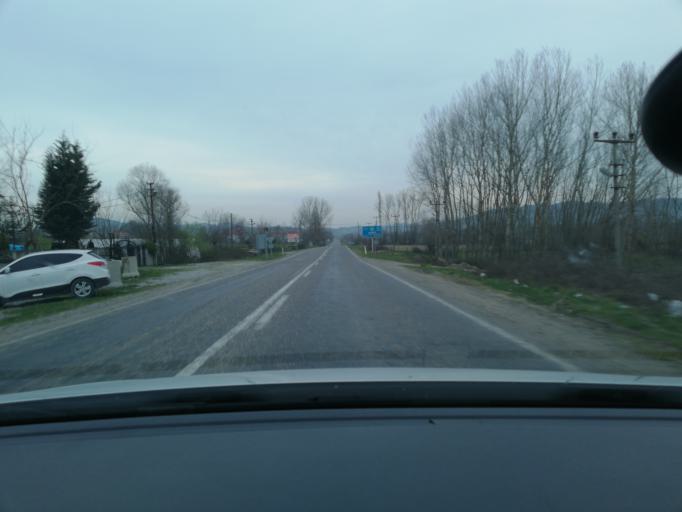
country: TR
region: Zonguldak
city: Saltukova
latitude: 41.5019
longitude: 32.0975
